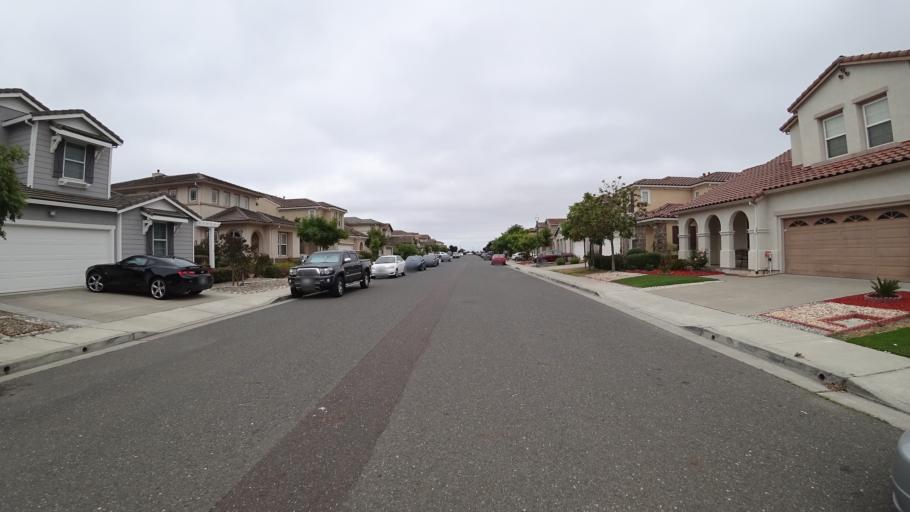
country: US
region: California
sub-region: Alameda County
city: Hayward
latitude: 37.6128
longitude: -122.0945
